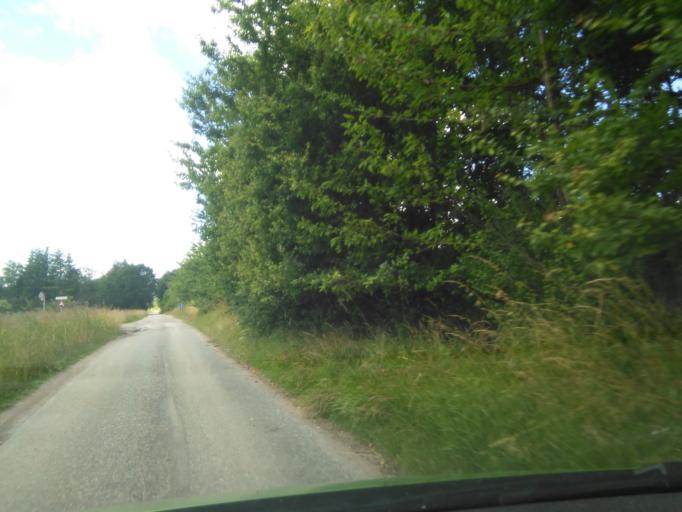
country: DK
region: Central Jutland
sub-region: Arhus Kommune
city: Logten
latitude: 56.1962
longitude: 10.3604
